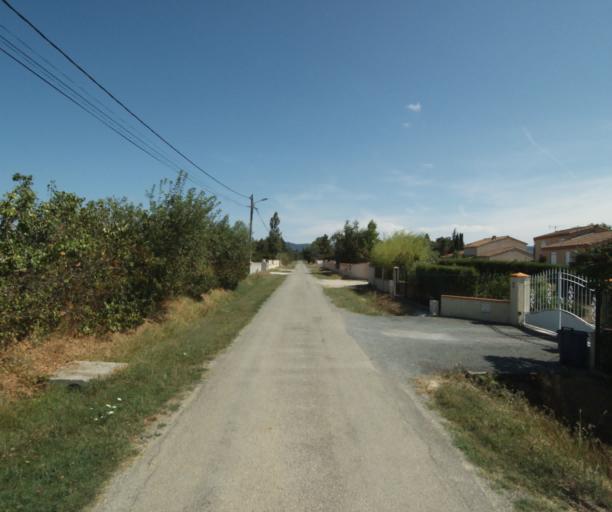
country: FR
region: Midi-Pyrenees
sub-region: Departement de la Haute-Garonne
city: Revel
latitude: 43.4848
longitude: 2.0034
